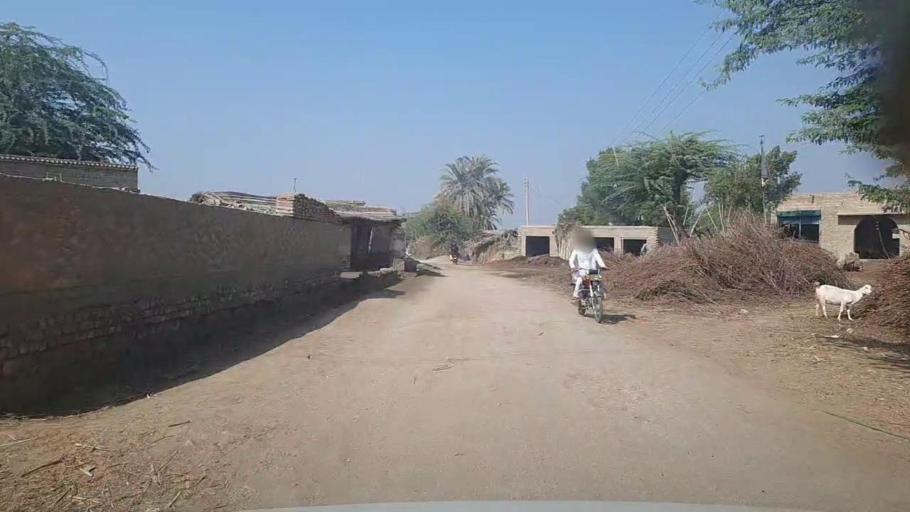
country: PK
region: Sindh
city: Karaundi
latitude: 26.9781
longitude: 68.4496
